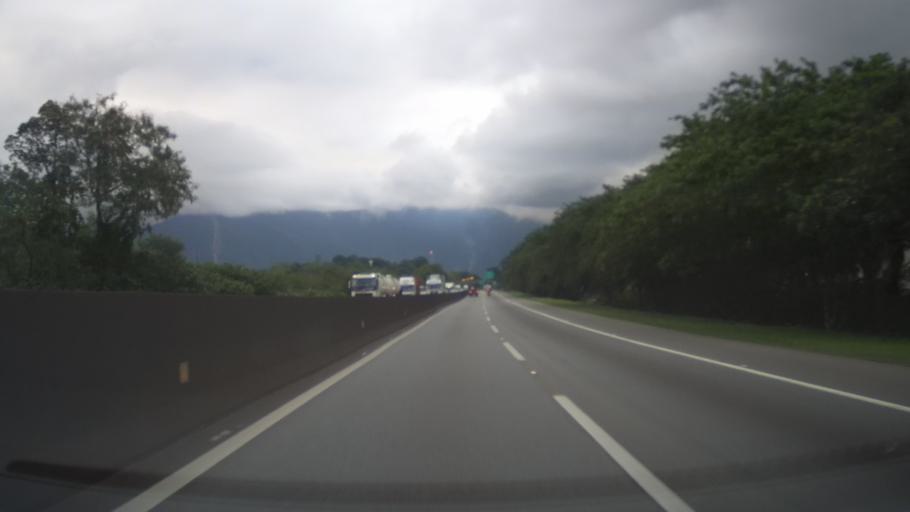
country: BR
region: Sao Paulo
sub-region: Cubatao
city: Cubatao
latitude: -23.9067
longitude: -46.4230
